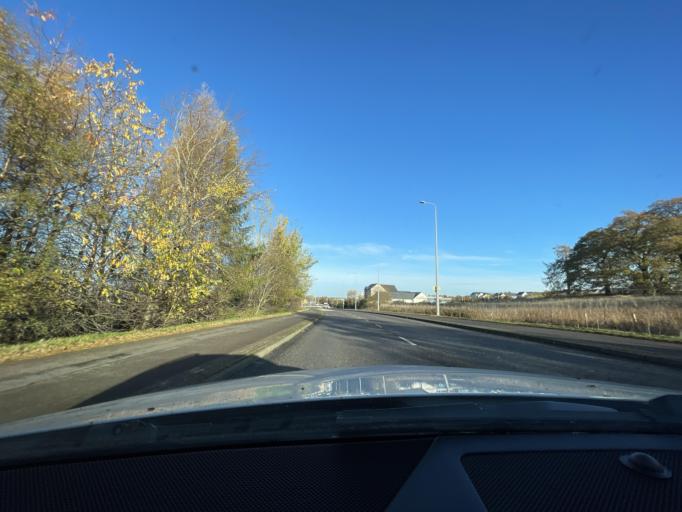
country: GB
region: Scotland
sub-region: Highland
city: Inverness
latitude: 57.4490
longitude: -4.2200
